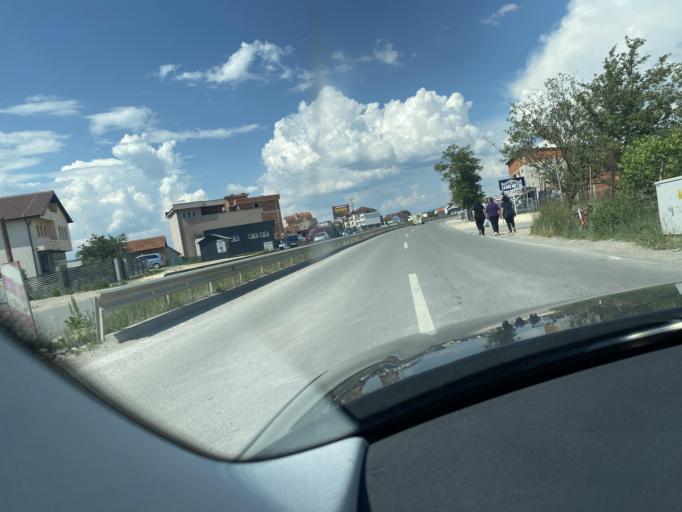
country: XK
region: Pristina
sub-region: Podujevo
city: Podujeva
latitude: 42.8873
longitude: 21.1815
